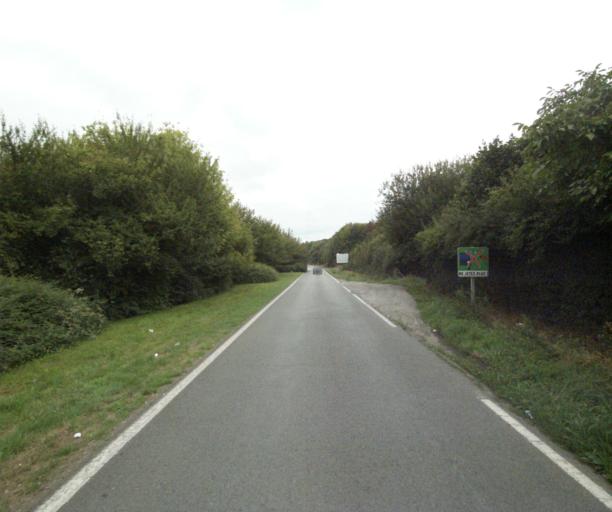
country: FR
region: Nord-Pas-de-Calais
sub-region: Departement du Nord
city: Lesquin
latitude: 50.5848
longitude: 3.1105
